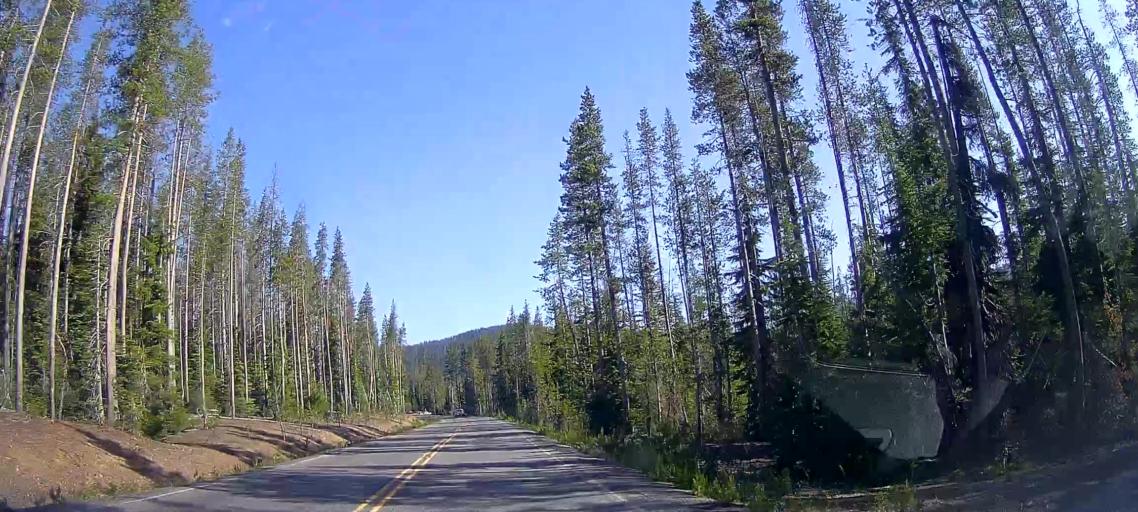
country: US
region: Oregon
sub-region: Jackson County
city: Shady Cove
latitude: 42.8560
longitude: -122.1532
